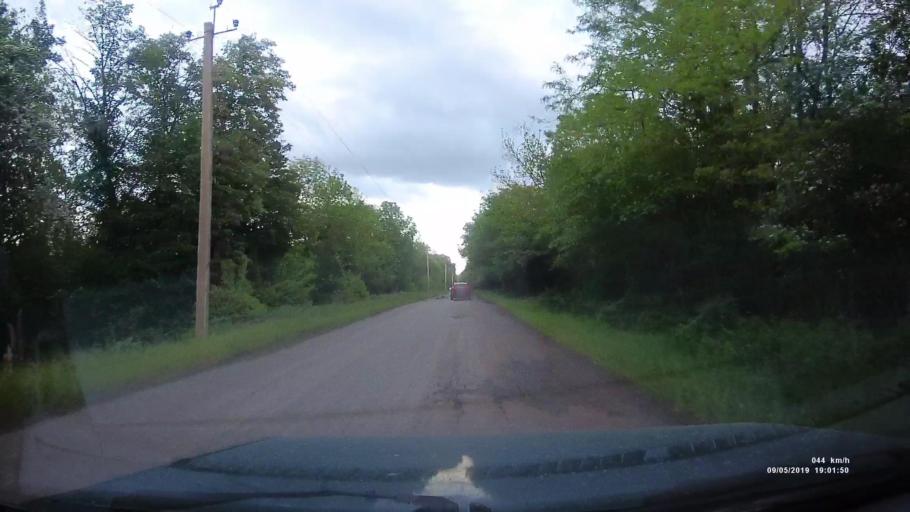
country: RU
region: Krasnodarskiy
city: Kanelovskaya
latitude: 46.7469
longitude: 39.1471
